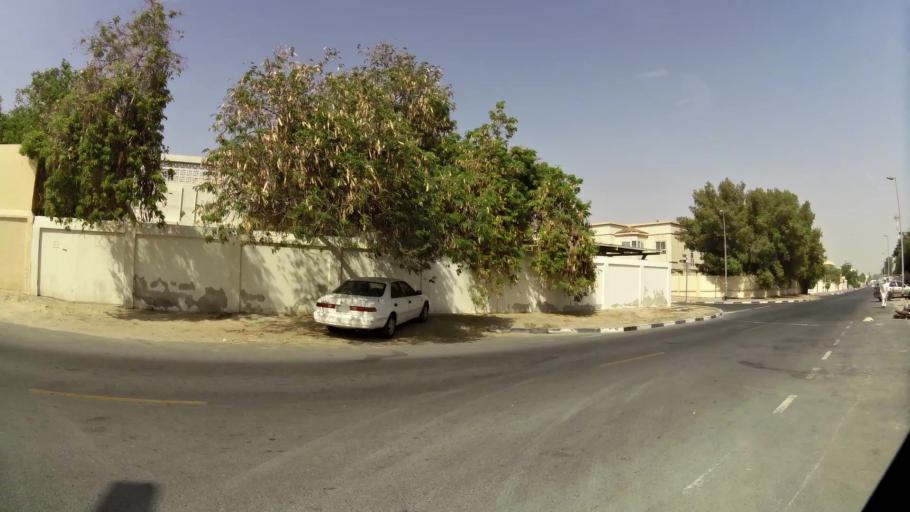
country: AE
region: Dubai
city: Dubai
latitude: 25.1713
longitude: 55.2542
